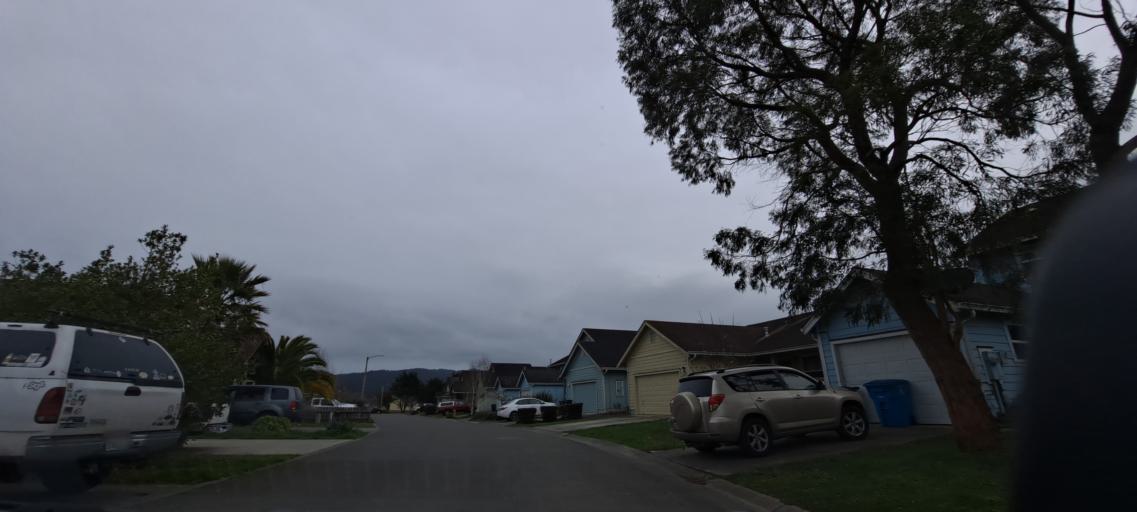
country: US
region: California
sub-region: Humboldt County
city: Arcata
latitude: 40.8713
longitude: -124.1051
